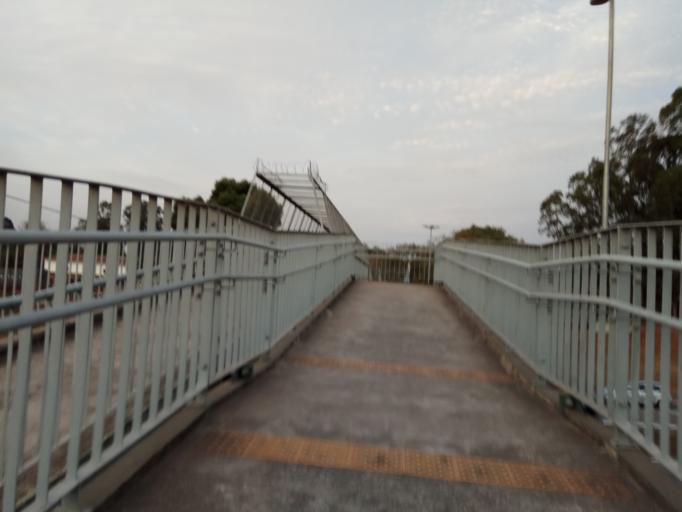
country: BR
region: Sao Paulo
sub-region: Piracicaba
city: Piracicaba
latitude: -22.7566
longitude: -47.5975
